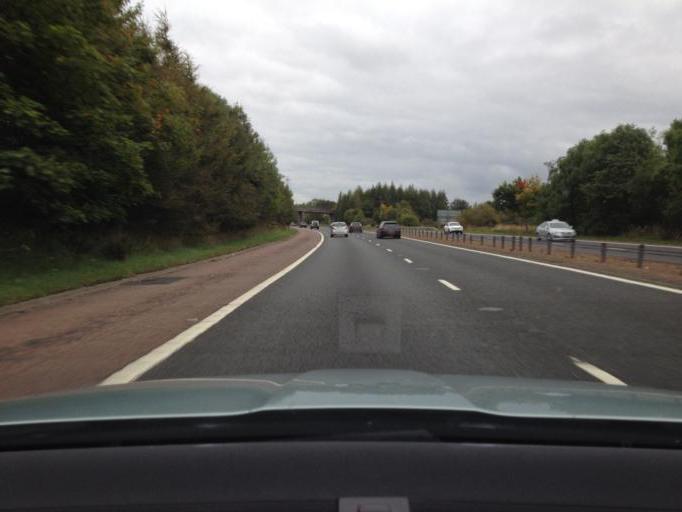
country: GB
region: Scotland
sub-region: Fife
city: Kelty
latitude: 56.1151
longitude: -3.3937
